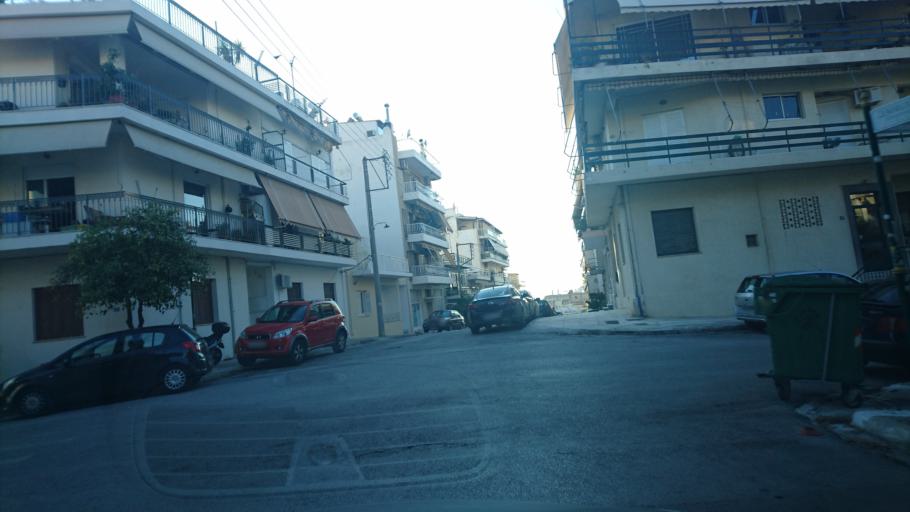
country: GR
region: Attica
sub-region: Nomarchia Athinas
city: Ilioupoli
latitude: 37.9407
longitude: 23.7635
